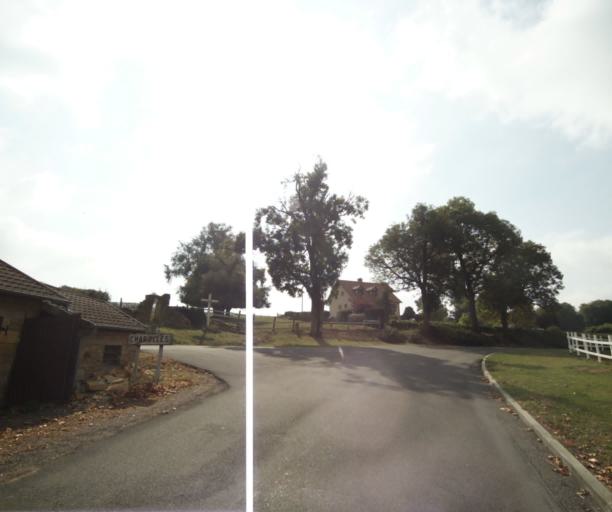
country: FR
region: Bourgogne
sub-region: Departement de Saone-et-Loire
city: Charolles
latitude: 46.4265
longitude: 4.2801
